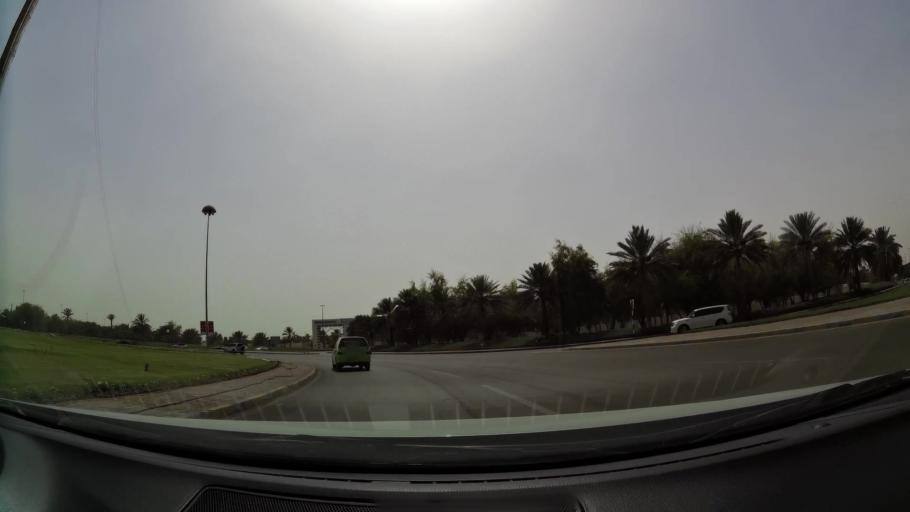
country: AE
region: Abu Dhabi
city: Al Ain
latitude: 24.1956
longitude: 55.6544
